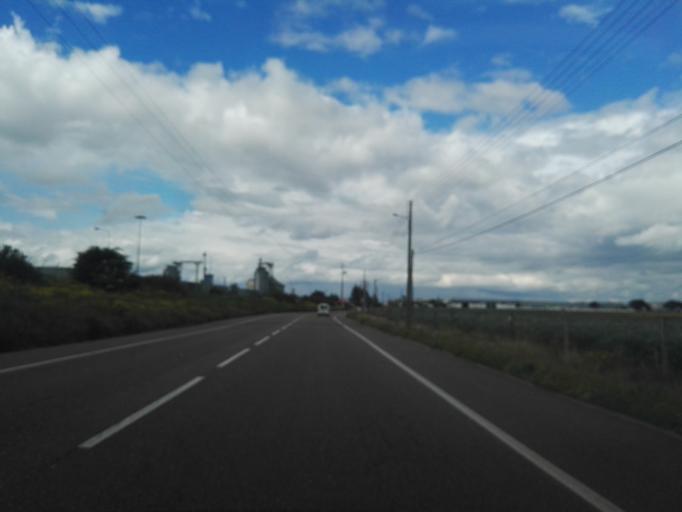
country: PT
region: Santarem
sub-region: Torres Novas
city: Riachos
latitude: 39.4375
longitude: -8.4958
